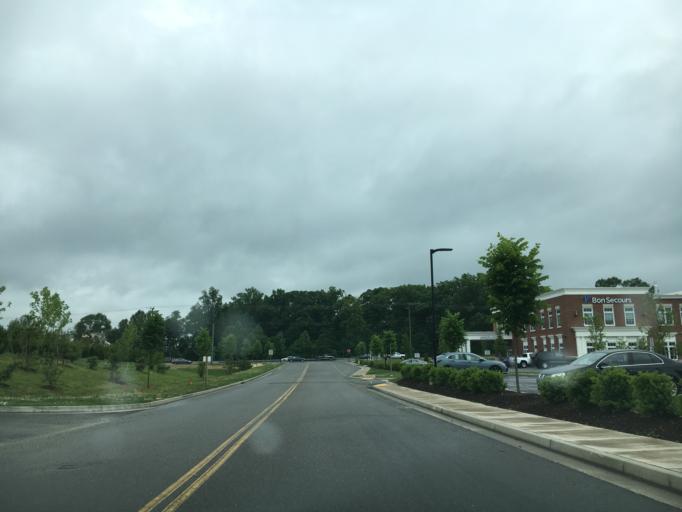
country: US
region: Virginia
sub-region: Henrico County
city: Short Pump
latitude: 37.6627
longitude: -77.6418
